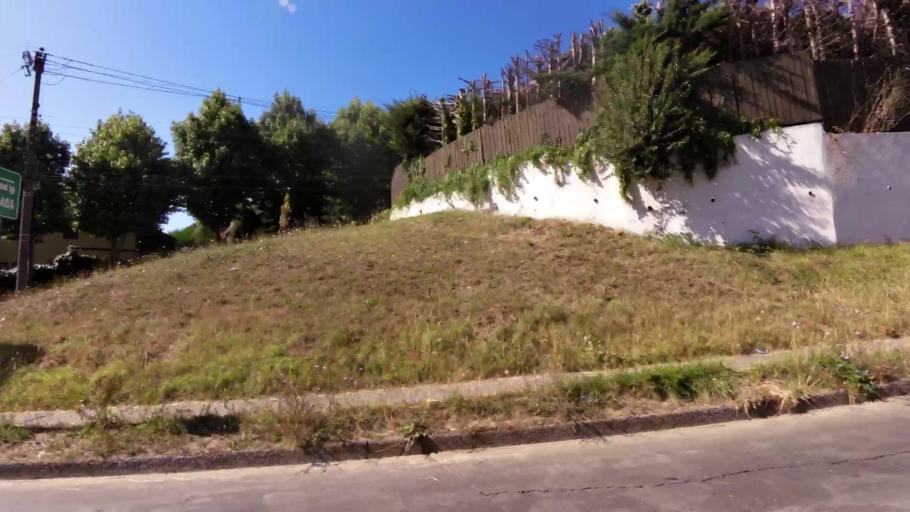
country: CL
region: Biobio
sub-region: Provincia de Concepcion
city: Concepcion
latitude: -36.7944
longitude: -73.0554
